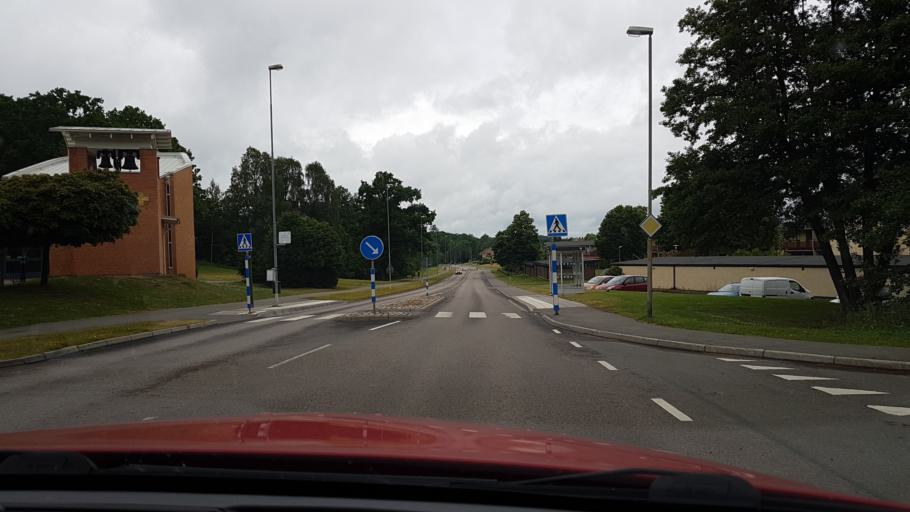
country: SE
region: Vaestra Goetaland
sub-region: Skovde Kommun
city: Skultorp
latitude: 58.3703
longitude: 13.8291
